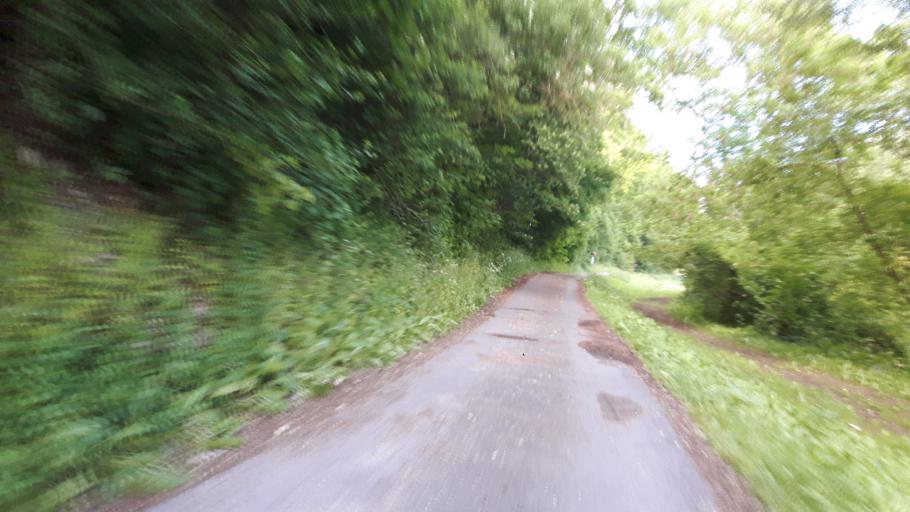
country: DE
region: Thuringia
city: Barchfeld
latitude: 50.8130
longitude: 11.1736
